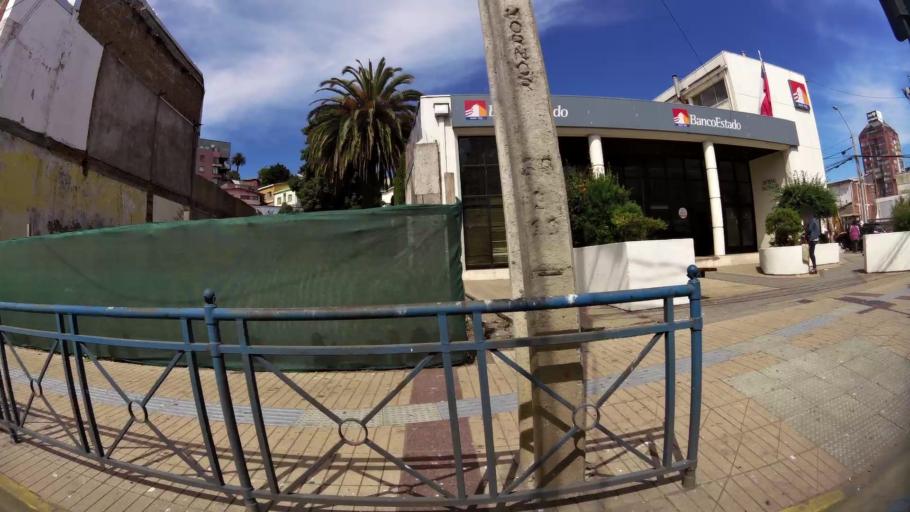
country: CL
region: Biobio
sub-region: Provincia de Concepcion
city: Talcahuano
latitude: -36.7150
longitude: -73.1109
